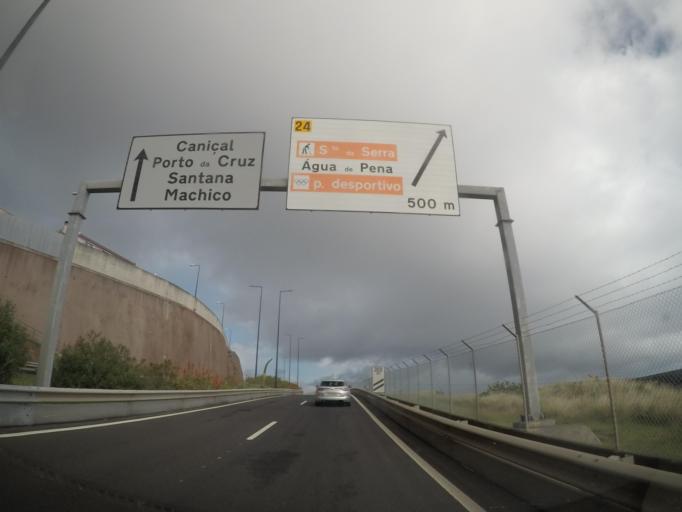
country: PT
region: Madeira
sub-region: Machico
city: Machico
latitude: 32.7052
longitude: -16.7662
